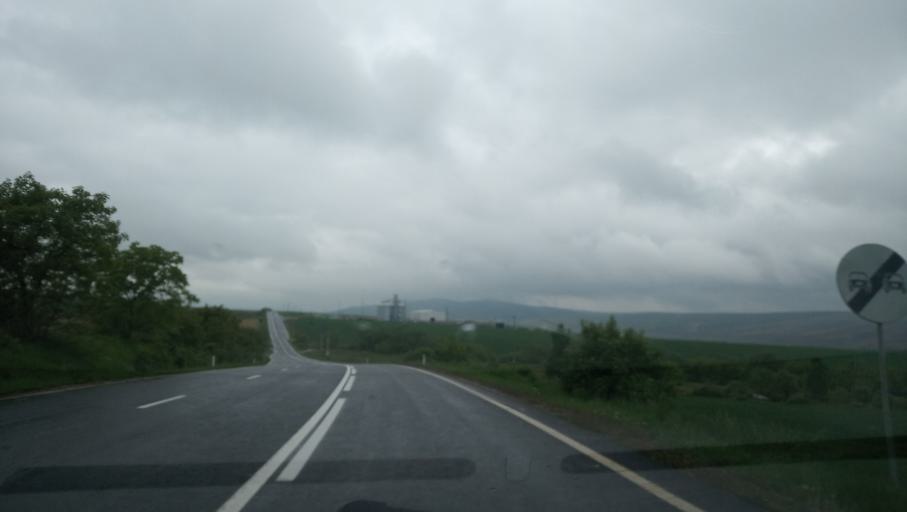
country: RO
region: Alba
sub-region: Comuna Cut
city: Cut
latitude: 45.9169
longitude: 23.7149
